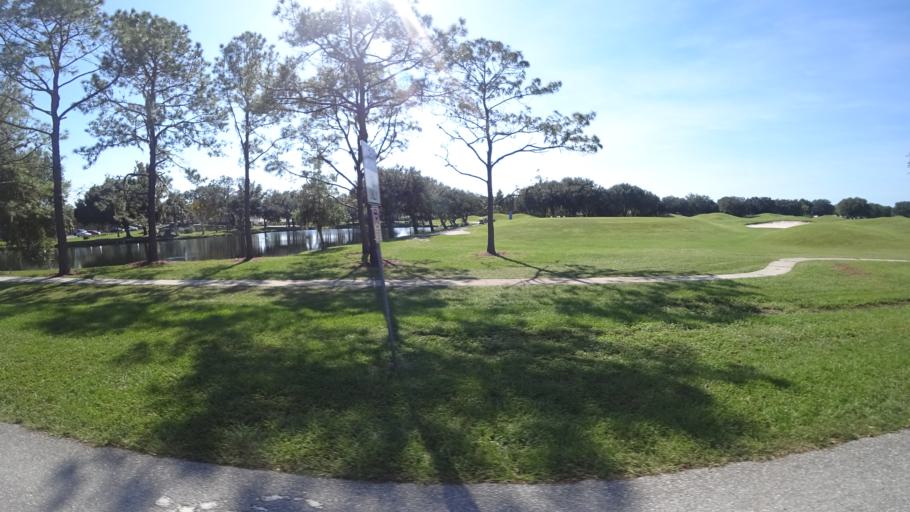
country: US
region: Florida
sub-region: Sarasota County
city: The Meadows
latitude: 27.4249
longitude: -82.4340
